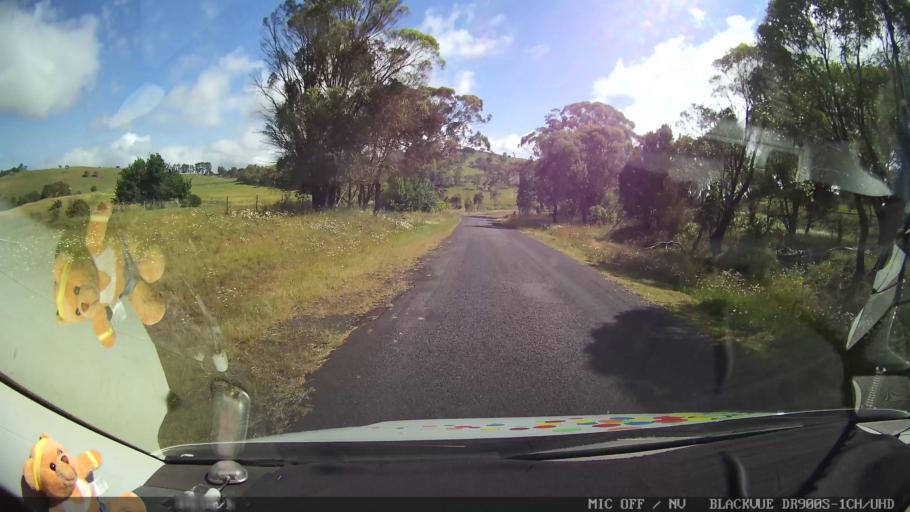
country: AU
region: New South Wales
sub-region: Guyra
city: Guyra
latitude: -30.0124
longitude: 151.6581
